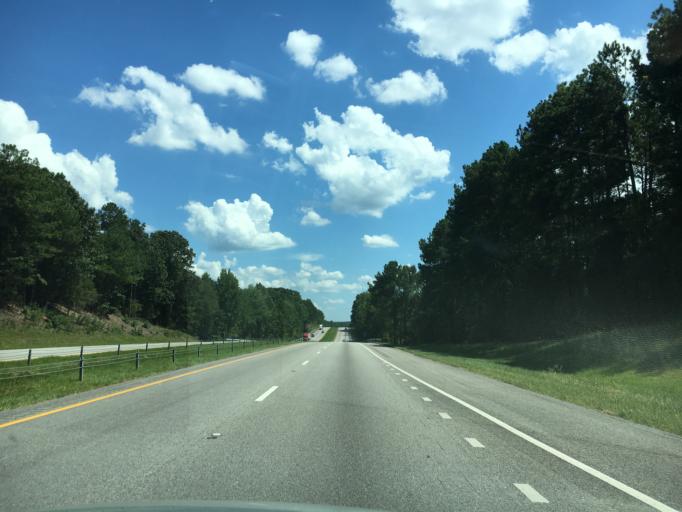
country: US
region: South Carolina
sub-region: Laurens County
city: Watts Mills
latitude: 34.6147
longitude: -81.8997
